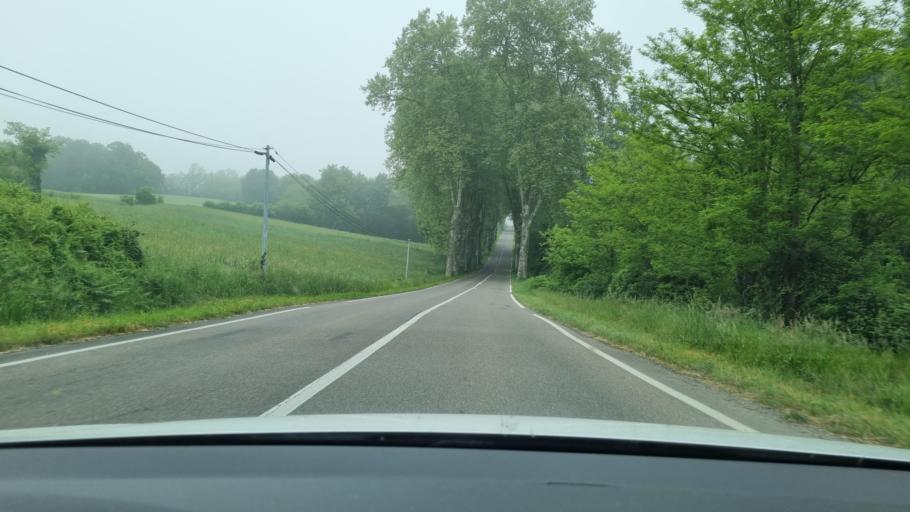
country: FR
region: Aquitaine
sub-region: Departement des Landes
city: Amou
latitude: 43.5580
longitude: -0.6660
